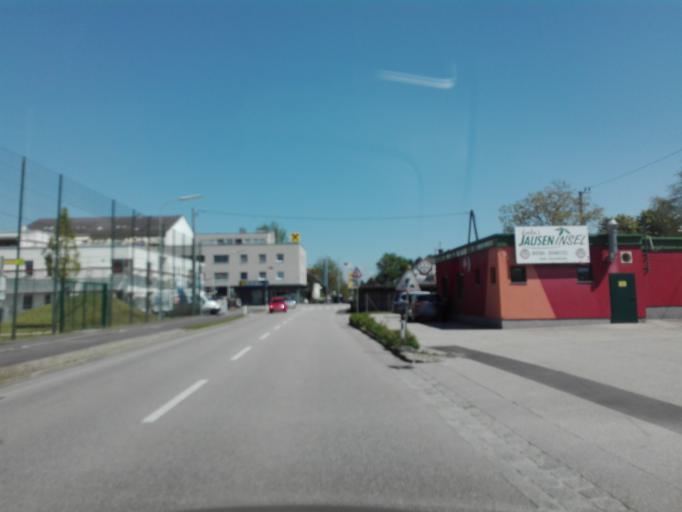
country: AT
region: Upper Austria
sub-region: Politischer Bezirk Linz-Land
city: Traun
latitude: 48.2362
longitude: 14.2635
